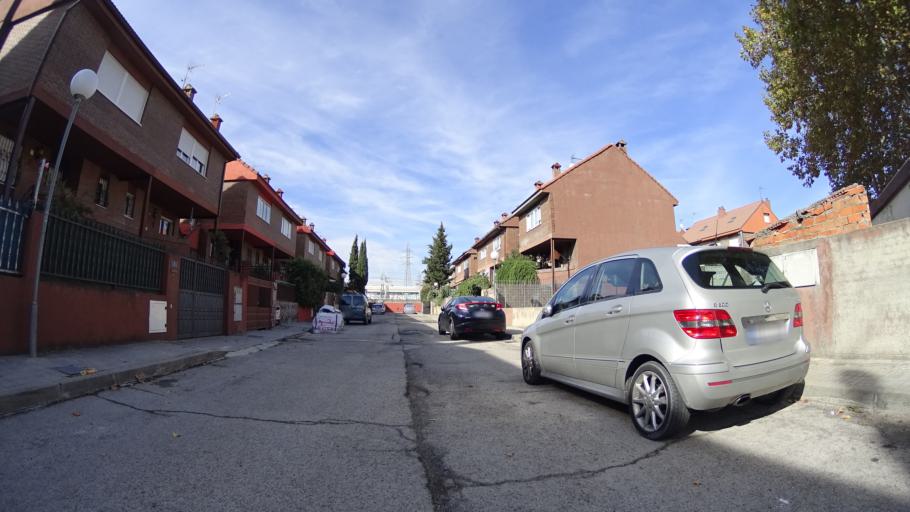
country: ES
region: Madrid
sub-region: Provincia de Madrid
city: Collado-Villalba
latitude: 40.6232
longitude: -4.0176
